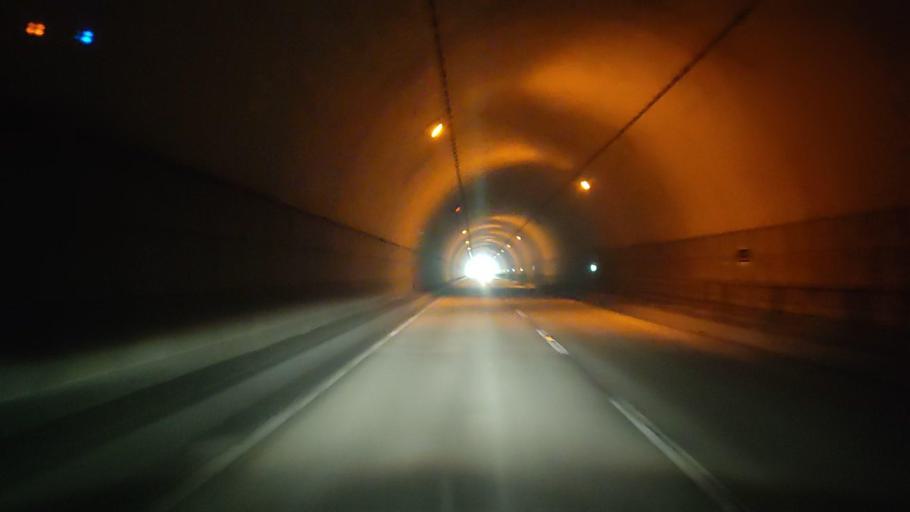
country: JP
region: Miyazaki
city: Nobeoka
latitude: 32.6734
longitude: 131.7708
